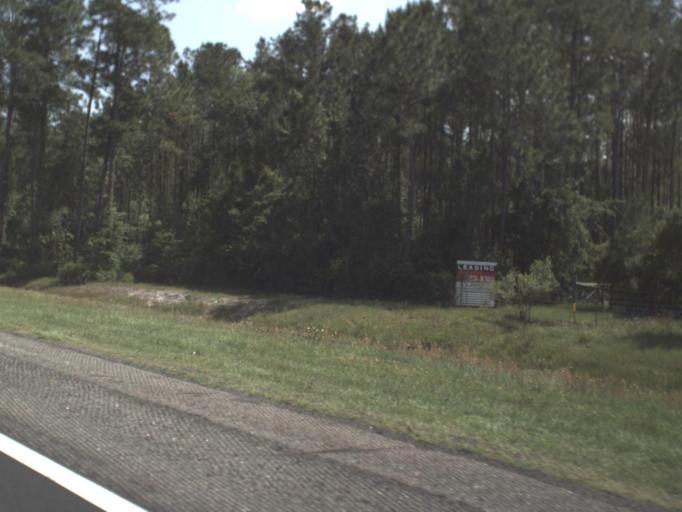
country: US
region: Florida
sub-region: Nassau County
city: Yulee
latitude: 30.5398
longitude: -81.6373
